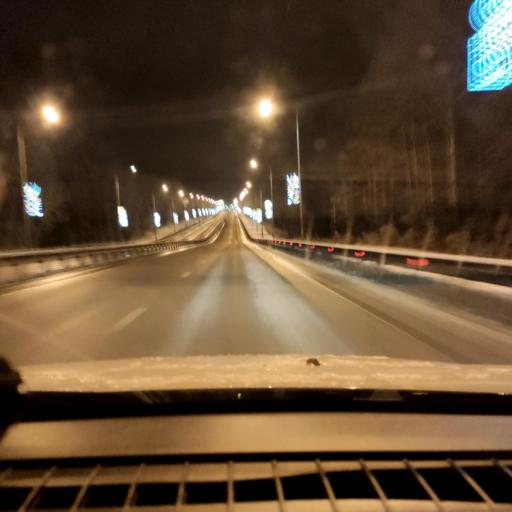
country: RU
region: Samara
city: Petra-Dubrava
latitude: 53.2881
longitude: 50.2494
